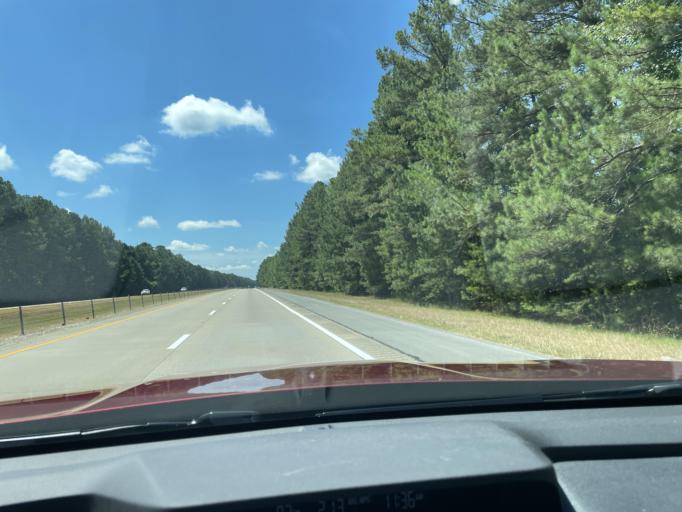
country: US
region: Arkansas
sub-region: Jefferson County
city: Redfield
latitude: 34.4279
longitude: -92.1930
